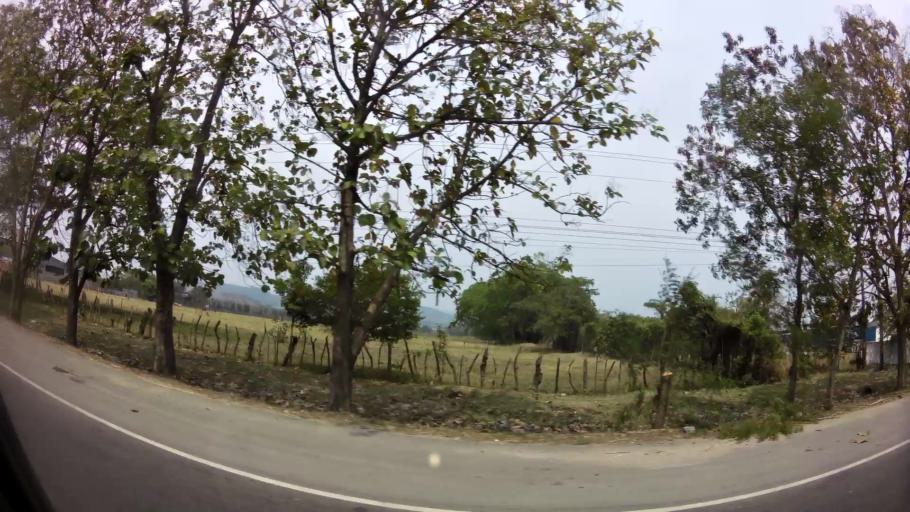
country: HN
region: Cortes
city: Nuevo Chamelecon
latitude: 15.3624
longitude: -87.9855
